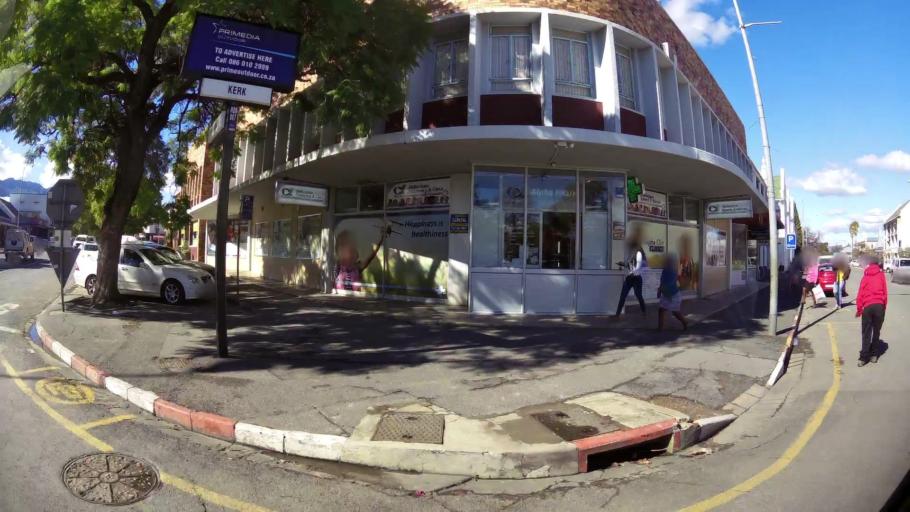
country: ZA
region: Western Cape
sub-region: Cape Winelands District Municipality
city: Ashton
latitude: -33.8036
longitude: 19.8816
